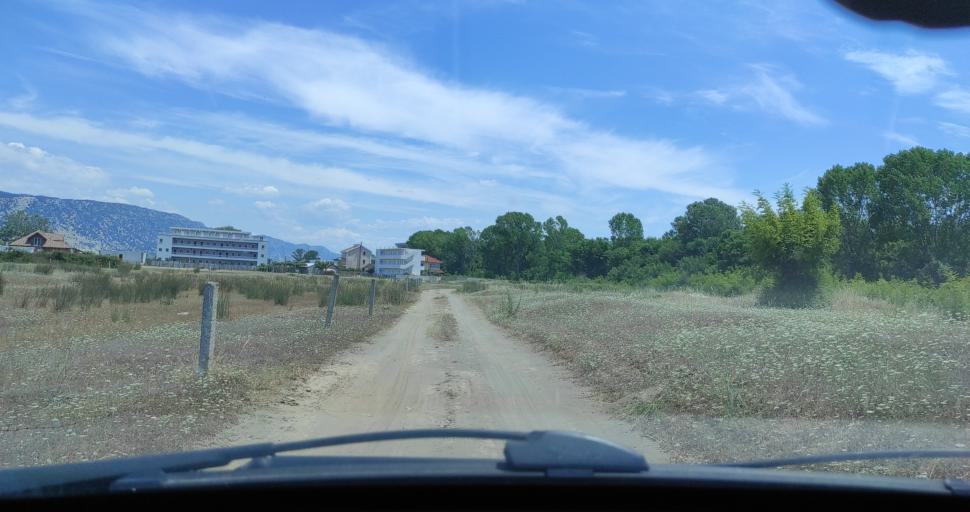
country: AL
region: Shkoder
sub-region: Rrethi i Shkodres
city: Velipoje
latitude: 41.8691
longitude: 19.3982
